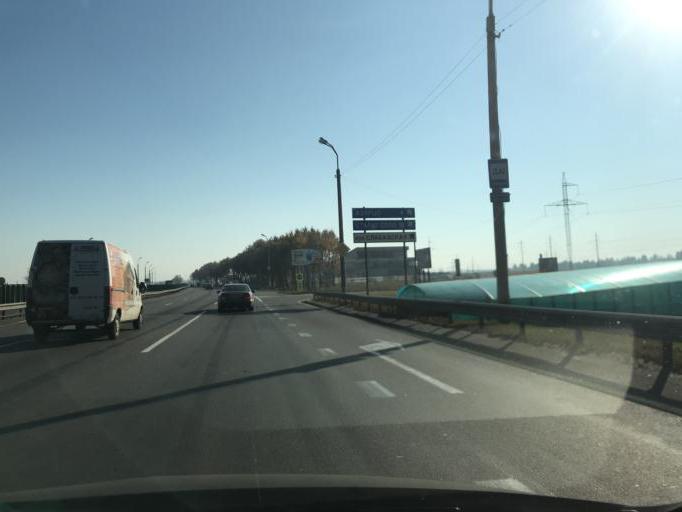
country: BY
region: Minsk
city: Malinovka
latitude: 53.8557
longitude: 27.4300
